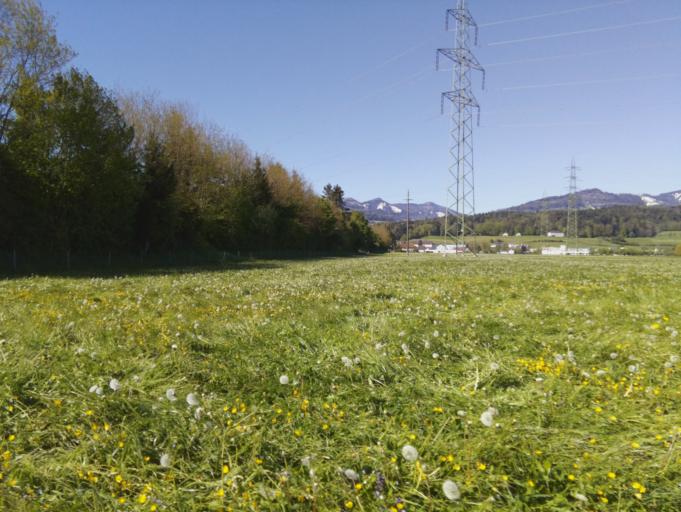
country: CH
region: Saint Gallen
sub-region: Wahlkreis See-Gaster
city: Schmerikon
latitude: 47.2201
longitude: 8.9632
